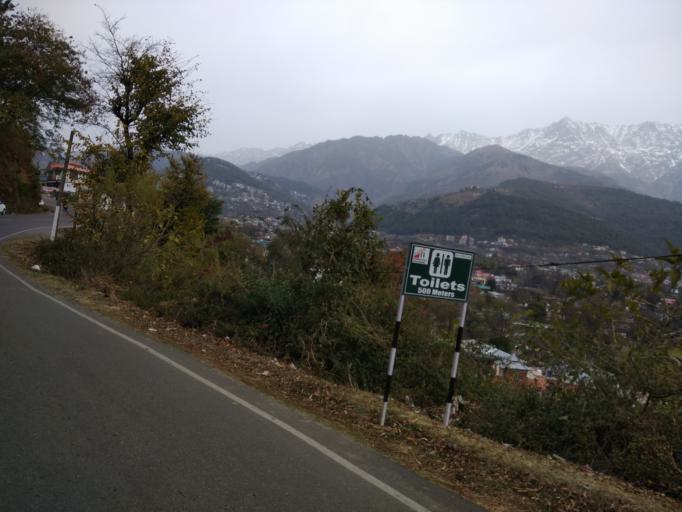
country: IN
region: Himachal Pradesh
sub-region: Kangra
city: Dharmsala
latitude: 32.2039
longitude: 76.3255
